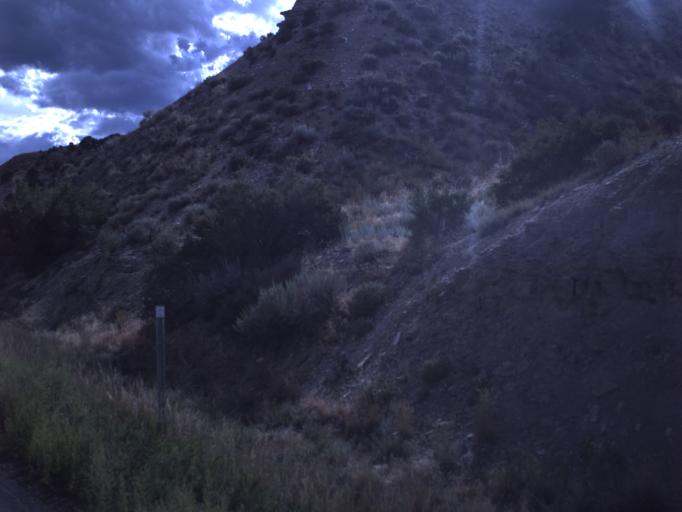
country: US
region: Utah
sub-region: Duchesne County
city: Duchesne
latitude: 40.1221
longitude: -110.4467
